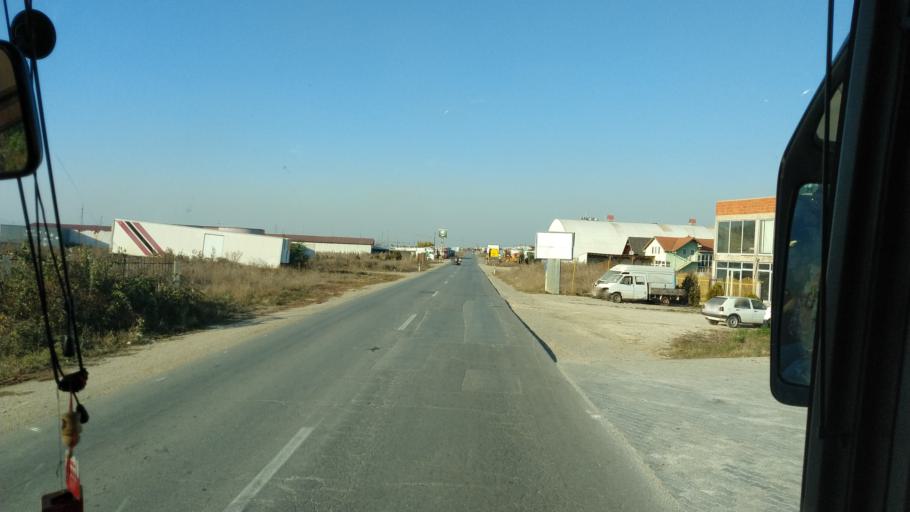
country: XK
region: Pristina
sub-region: Lipjan
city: Lipljan
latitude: 42.5179
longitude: 21.1125
